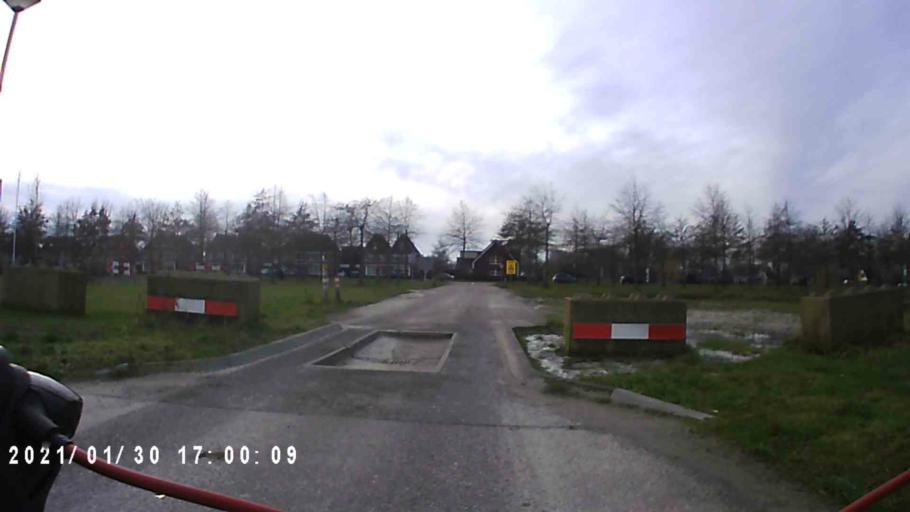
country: NL
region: Groningen
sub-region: Gemeente Leek
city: Leek
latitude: 53.1494
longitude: 6.3738
